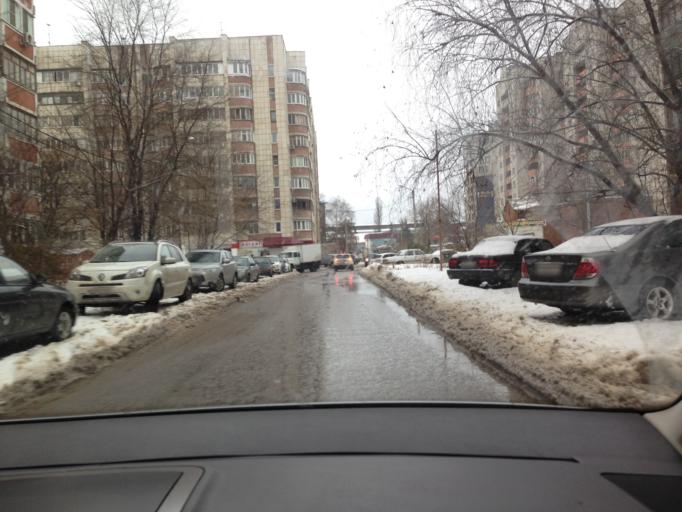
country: RU
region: Voronezj
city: Voronezh
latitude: 51.6719
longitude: 39.1833
